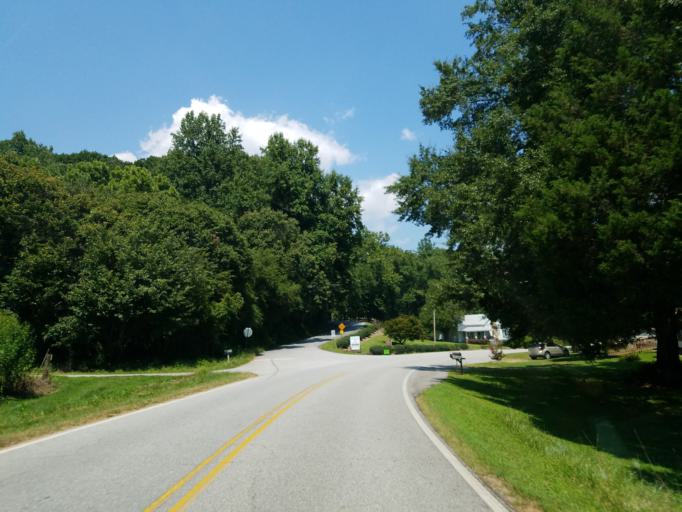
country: US
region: Georgia
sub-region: Lumpkin County
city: Dahlonega
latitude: 34.6580
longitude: -83.9082
